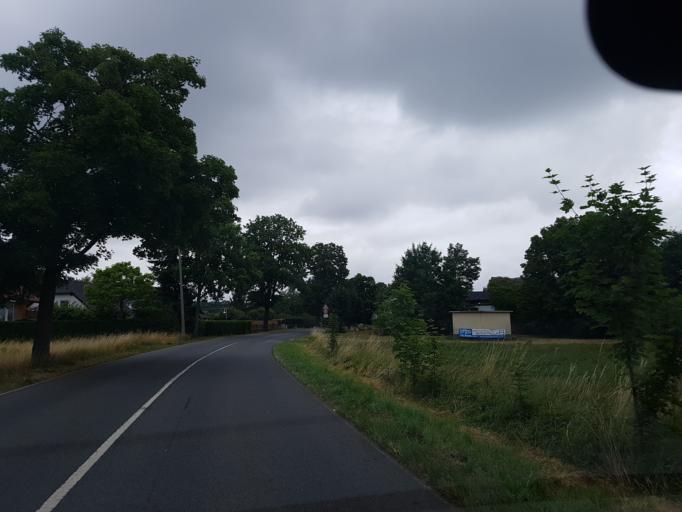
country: DE
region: Brandenburg
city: Luckau
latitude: 51.8400
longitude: 13.6899
